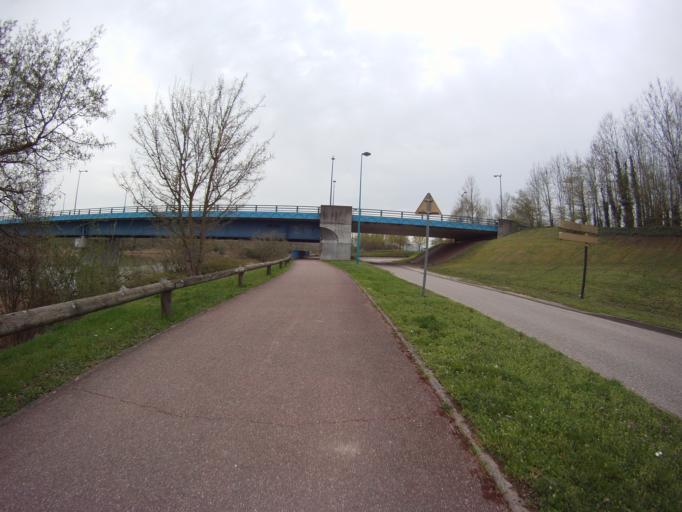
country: FR
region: Lorraine
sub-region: Departement de Meurthe-et-Moselle
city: Tomblaine
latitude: 48.6783
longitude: 6.2084
